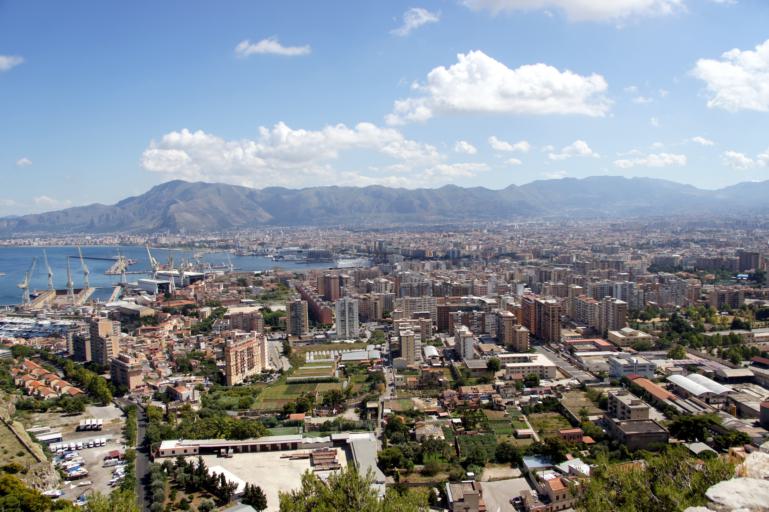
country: IT
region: Sicily
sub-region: Palermo
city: Palermo
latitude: 38.1535
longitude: 13.3611
